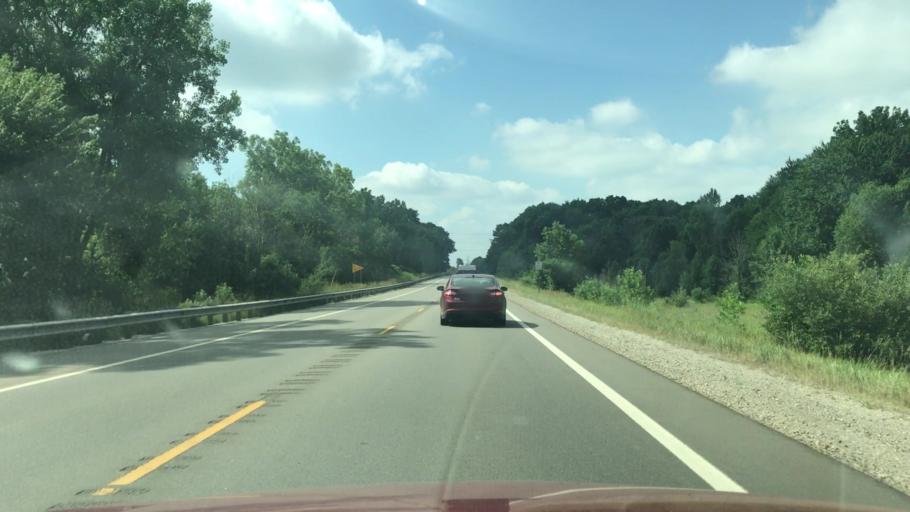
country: US
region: Michigan
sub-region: Kent County
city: Sparta
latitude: 43.1851
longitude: -85.7202
